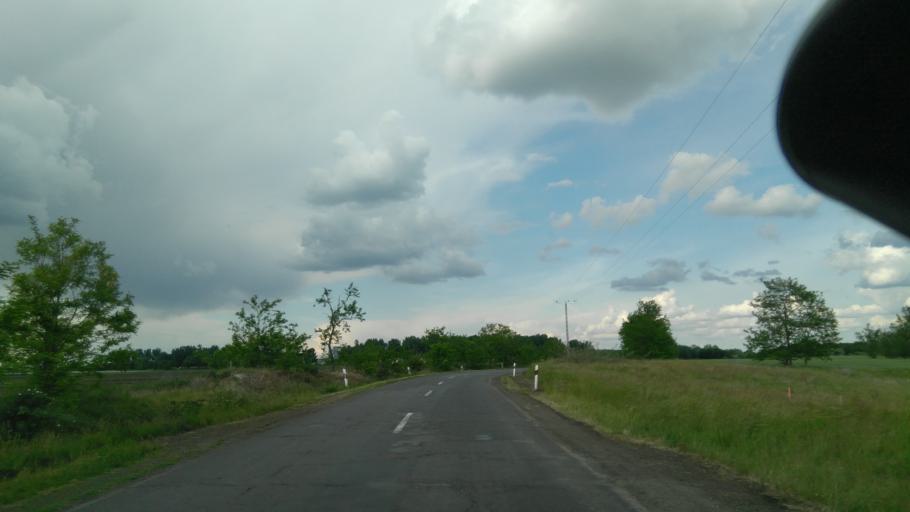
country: HU
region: Bekes
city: Dombegyhaz
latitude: 46.3290
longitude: 21.0973
